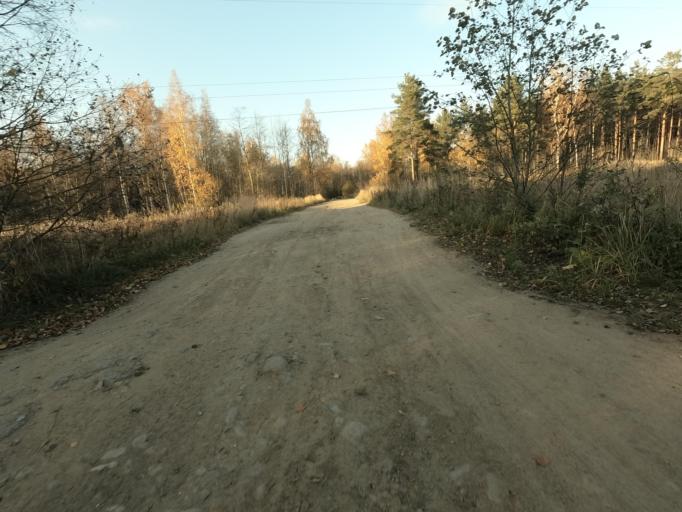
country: RU
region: Leningrad
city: Sinyavino
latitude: 59.8763
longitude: 31.0404
